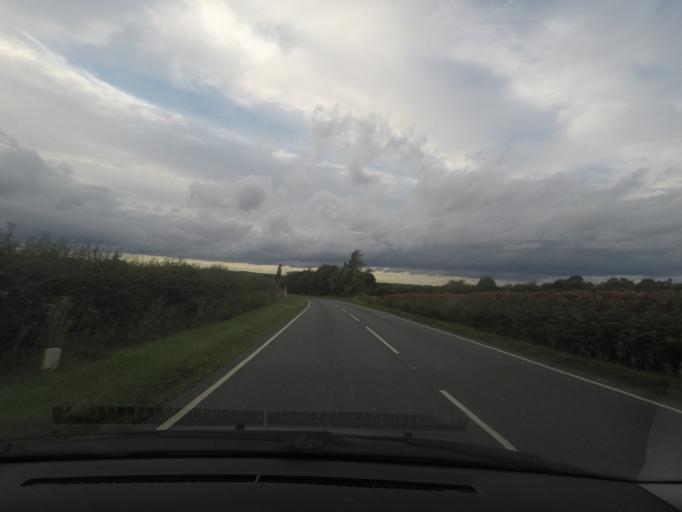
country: GB
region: England
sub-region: Lincolnshire
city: Burwell
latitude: 53.2617
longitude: 0.0899
